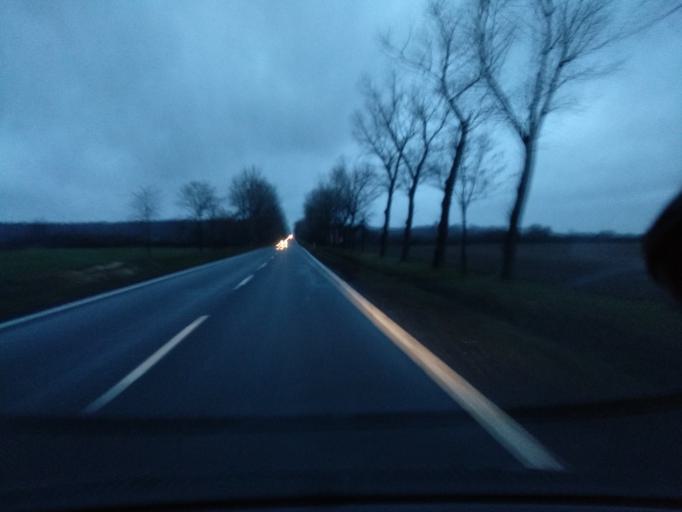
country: PL
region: Lower Silesian Voivodeship
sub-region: Powiat legnicki
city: Prochowice
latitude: 51.2402
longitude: 16.4144
